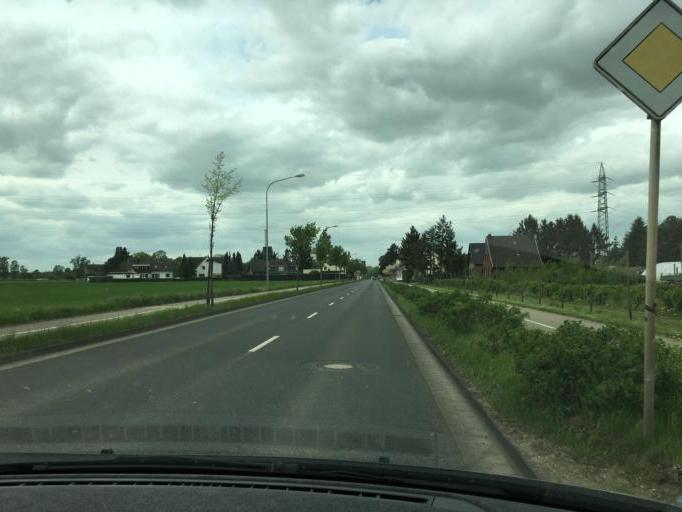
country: DE
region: North Rhine-Westphalia
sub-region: Regierungsbezirk Koln
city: Euskirchen
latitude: 50.6543
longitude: 6.8190
